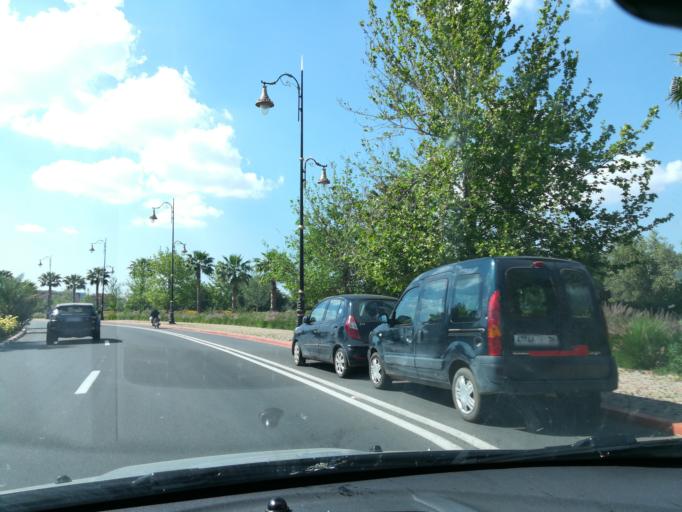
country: MA
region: Marrakech-Tensift-Al Haouz
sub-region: Marrakech
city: Marrakesh
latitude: 31.6151
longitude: -8.0044
